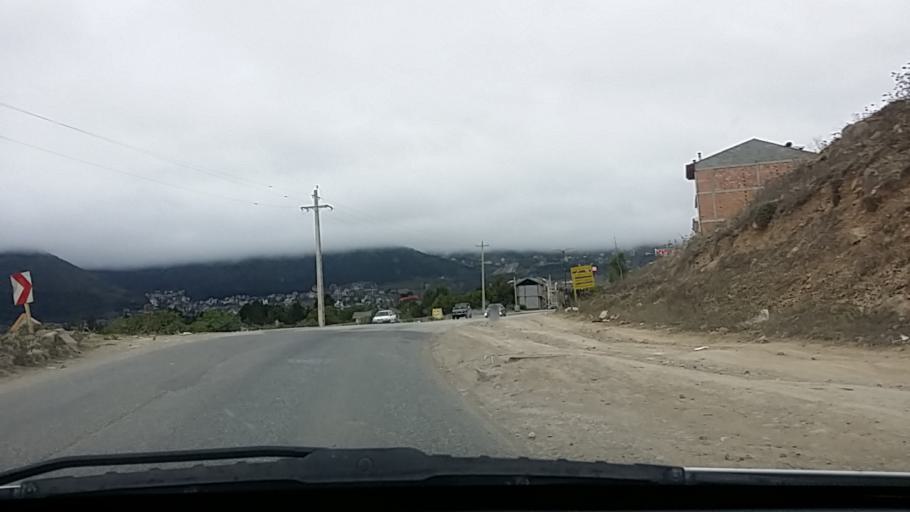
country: IR
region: Mazandaran
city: `Abbasabad
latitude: 36.5139
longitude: 51.1599
